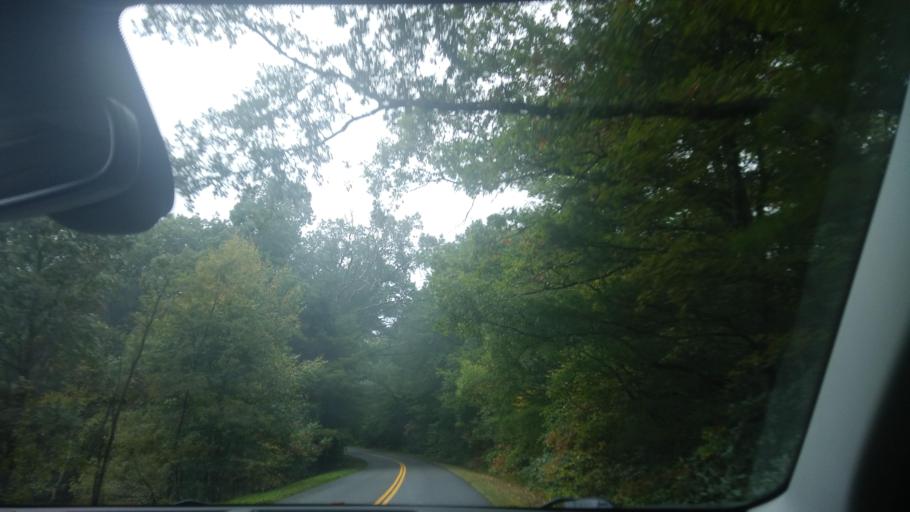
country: US
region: North Carolina
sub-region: Mitchell County
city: Spruce Pine
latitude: 35.8864
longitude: -81.9808
